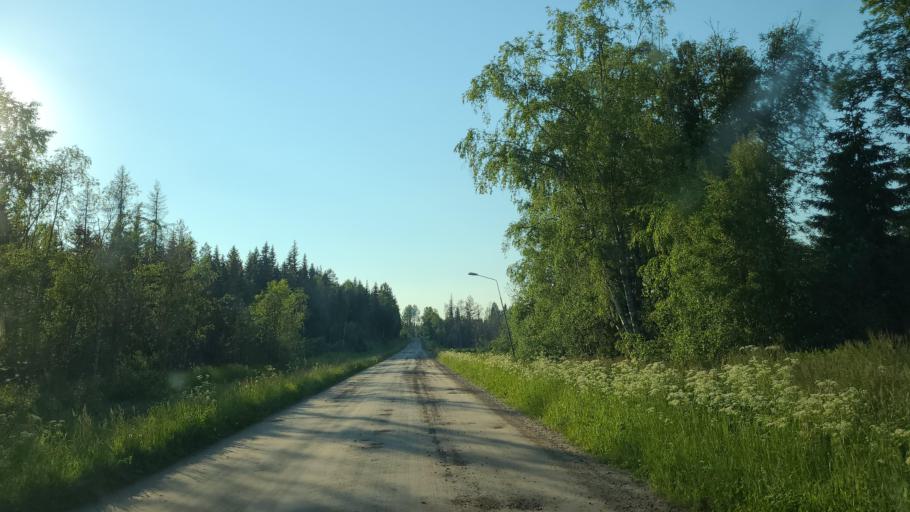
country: SE
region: Vaesterbotten
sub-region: Skelleftea Kommun
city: Burea
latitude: 64.4067
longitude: 21.3613
